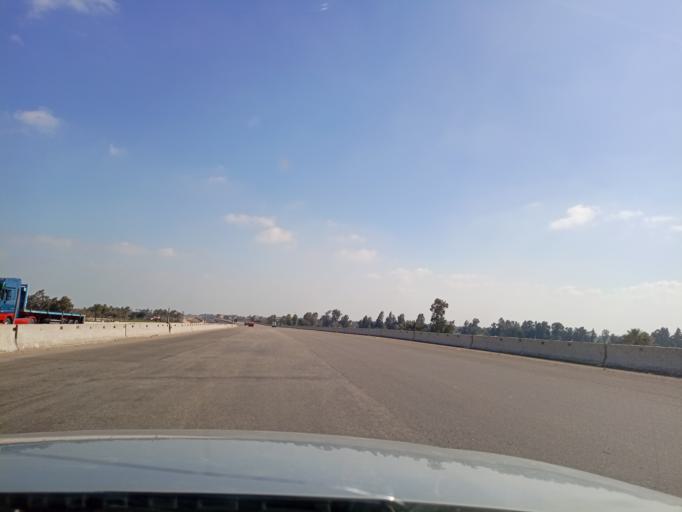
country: EG
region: Eastern Province
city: Mashtul as Suq
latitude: 30.4589
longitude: 31.3424
